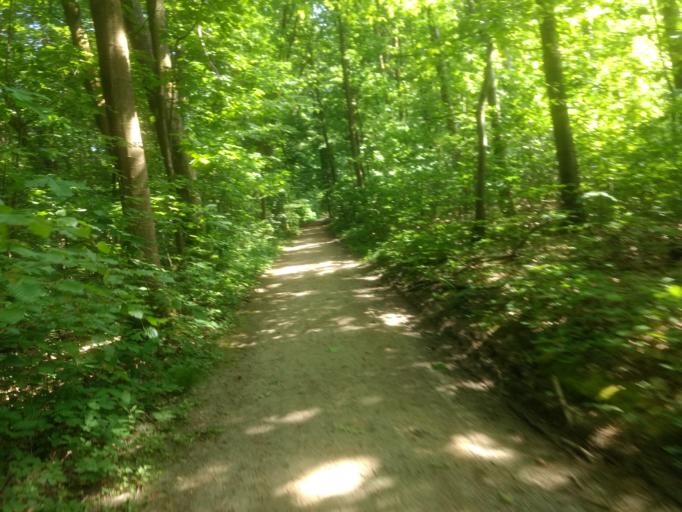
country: BE
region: Flanders
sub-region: Provincie Vlaams-Brabant
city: Oud-Heverlee
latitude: 50.8359
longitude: 4.6735
